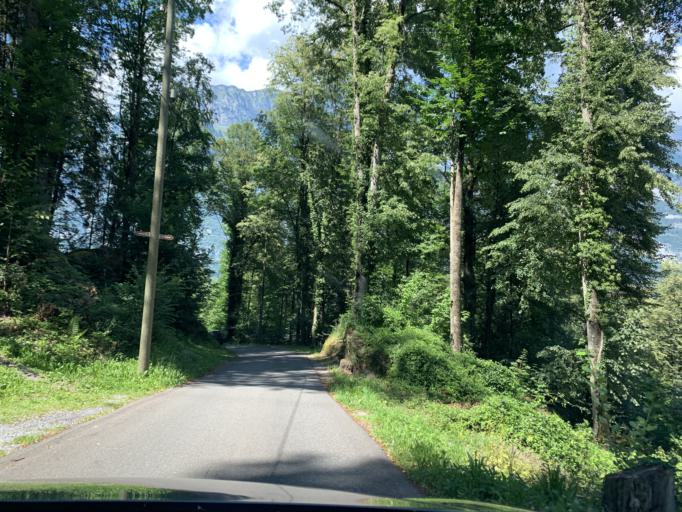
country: CH
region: Saint Gallen
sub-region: Wahlkreis Sarganserland
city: Quarten
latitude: 47.1083
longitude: 9.2130
